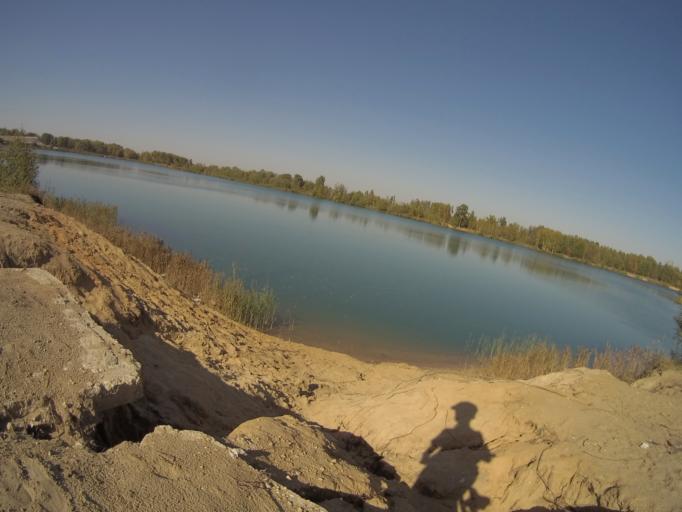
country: RU
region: Vladimir
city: Raduzhnyy
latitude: 56.0295
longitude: 40.3336
